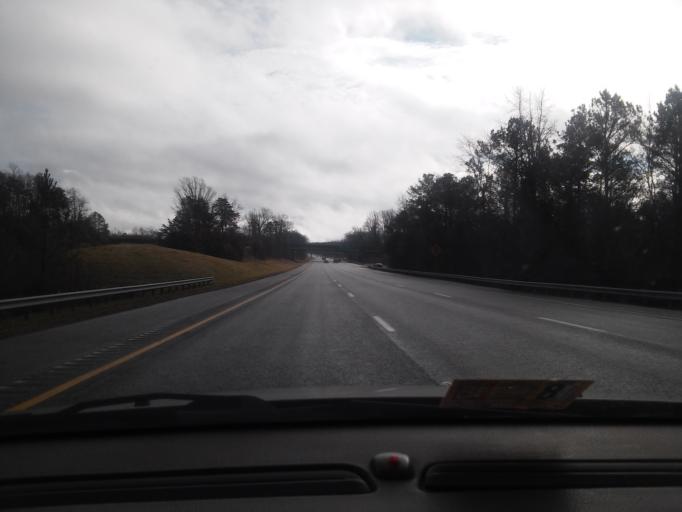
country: US
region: Virginia
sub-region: Henrico County
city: Short Pump
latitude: 37.6364
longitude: -77.5774
